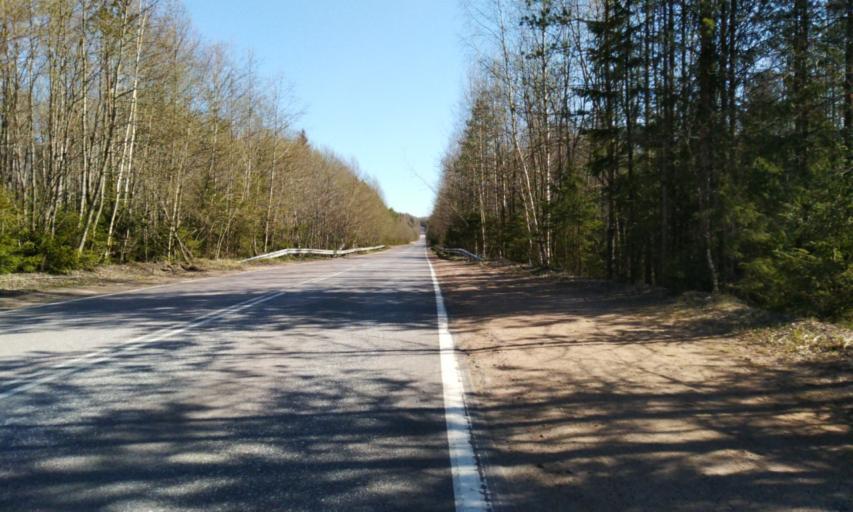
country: RU
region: Leningrad
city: Garbolovo
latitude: 60.3773
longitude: 30.4591
